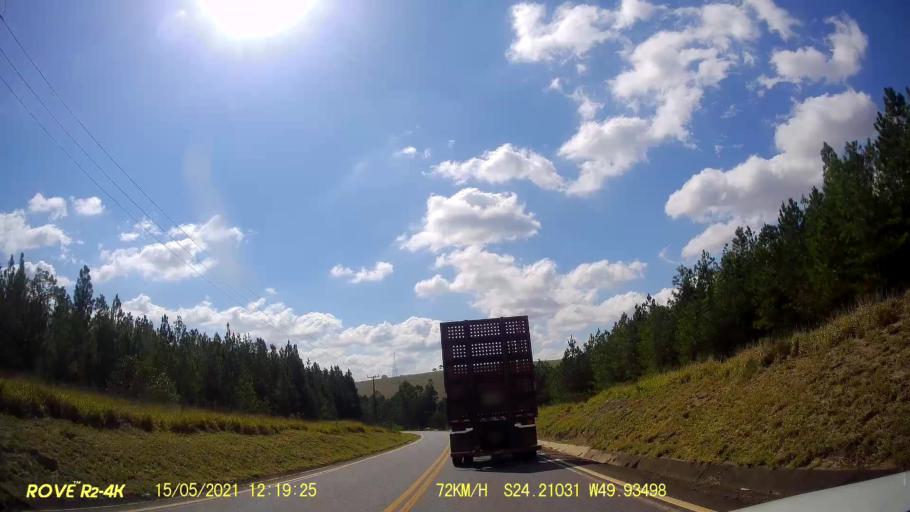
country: BR
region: Parana
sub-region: Jaguariaiva
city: Jaguariaiva
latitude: -24.2094
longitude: -49.9346
